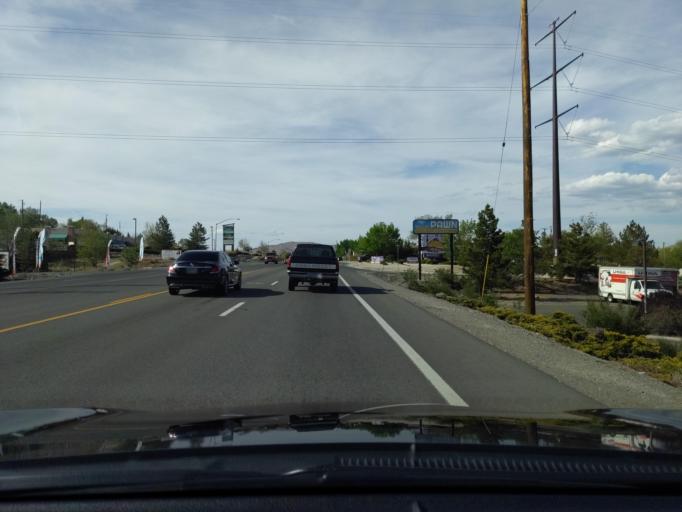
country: US
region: Nevada
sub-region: Washoe County
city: Sun Valley
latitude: 39.5740
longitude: -119.7811
